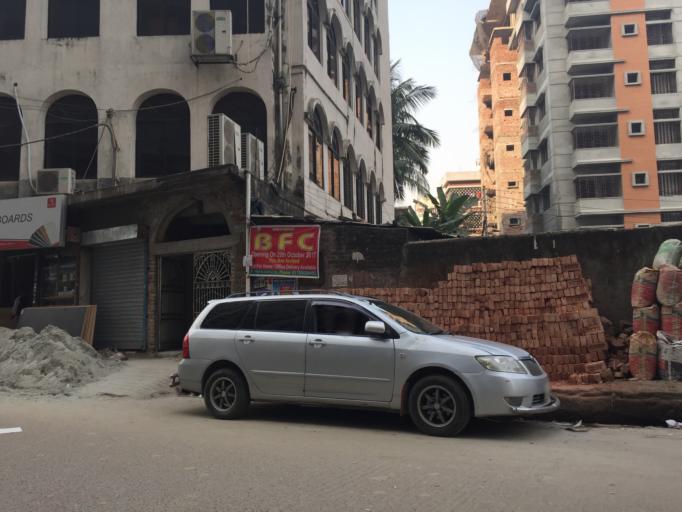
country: BD
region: Dhaka
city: Paltan
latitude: 23.7319
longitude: 90.4142
